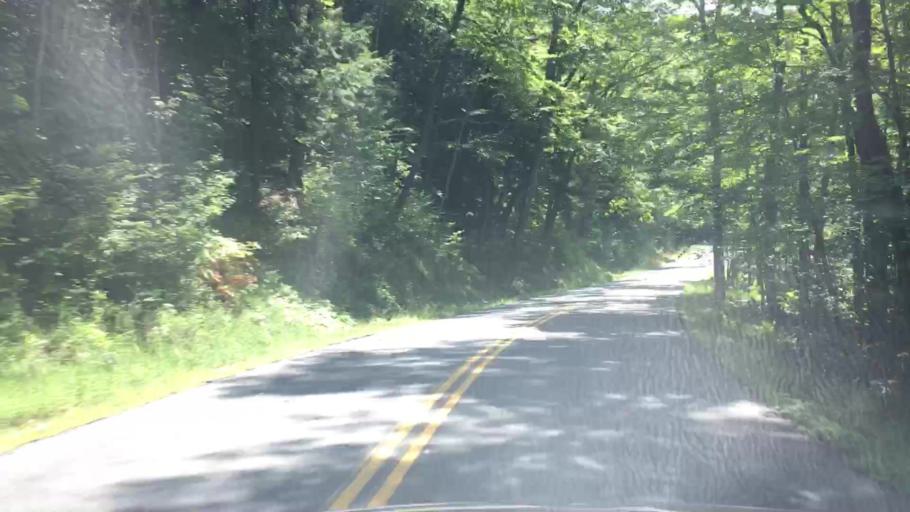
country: US
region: Vermont
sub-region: Windham County
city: West Brattleboro
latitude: 42.8048
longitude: -72.7039
